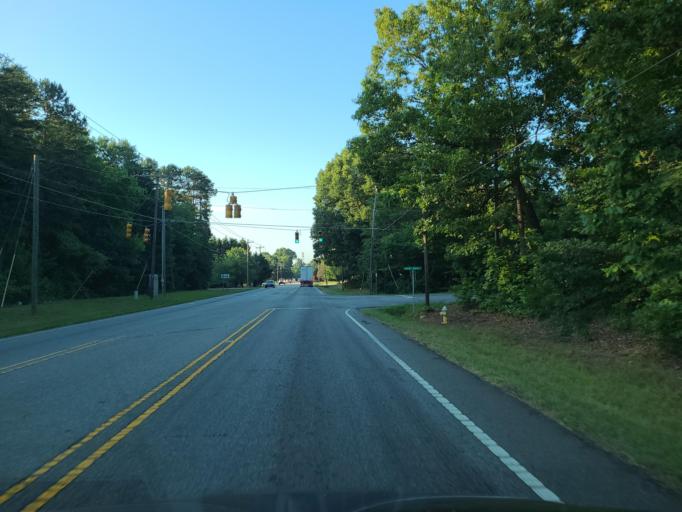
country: US
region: North Carolina
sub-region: Catawba County
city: Mountain View
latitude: 35.6646
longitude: -81.3818
